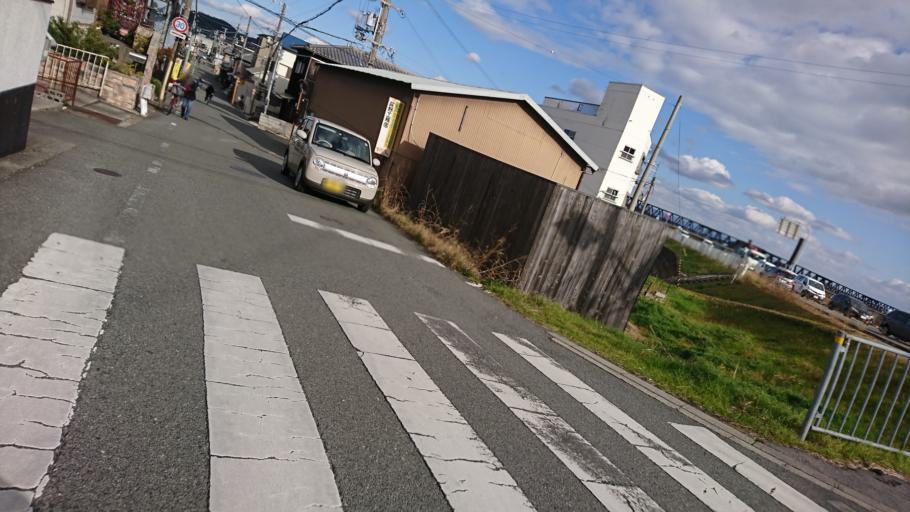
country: JP
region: Hyogo
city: Kakogawacho-honmachi
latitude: 34.7744
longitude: 134.8271
